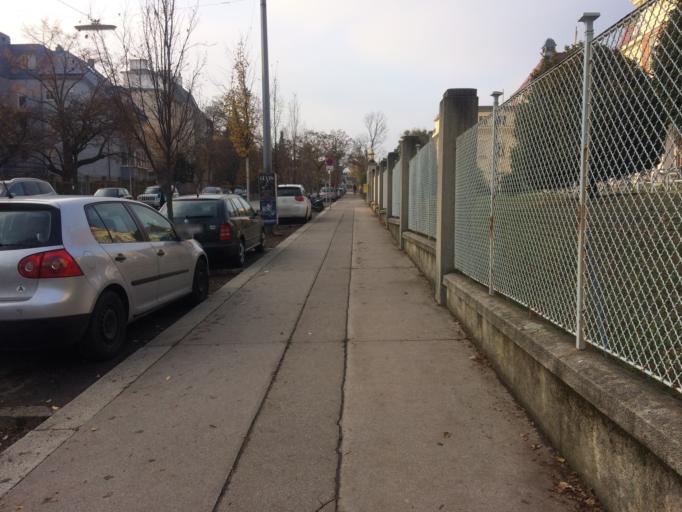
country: AT
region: Vienna
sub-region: Wien Stadt
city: Vienna
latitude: 48.2372
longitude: 16.3324
